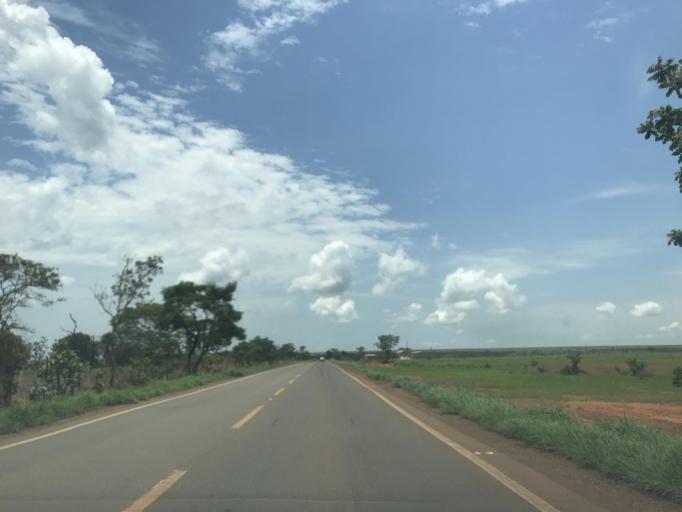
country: BR
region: Goias
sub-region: Luziania
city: Luziania
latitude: -16.4709
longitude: -48.2129
